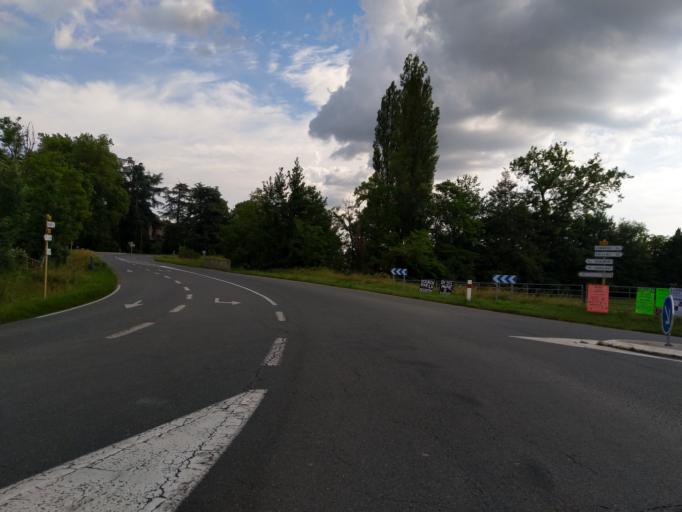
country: FR
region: Midi-Pyrenees
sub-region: Departement du Tarn
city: Realmont
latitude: 43.8031
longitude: 2.1534
